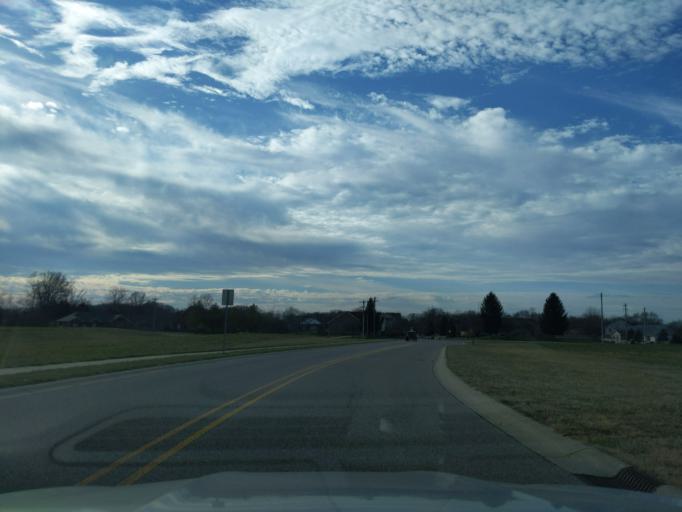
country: US
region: Indiana
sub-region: Decatur County
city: Greensburg
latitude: 39.3201
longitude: -85.4685
